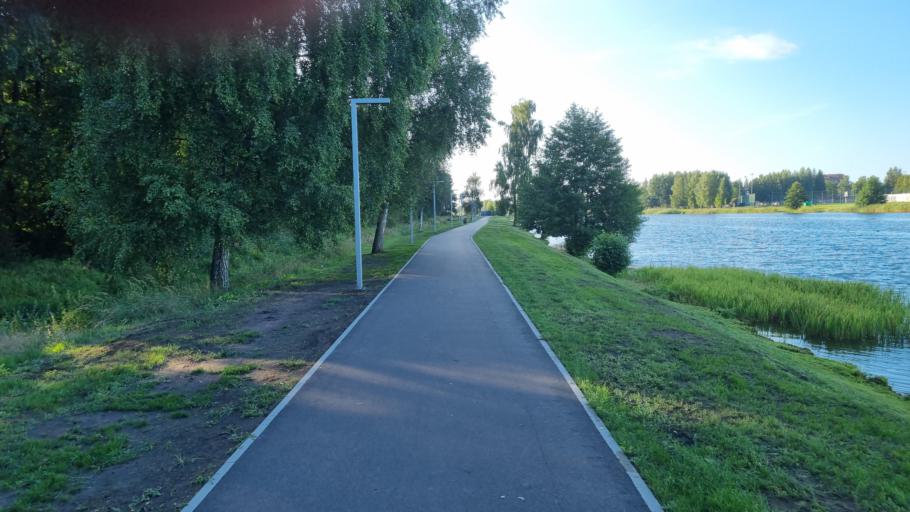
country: LV
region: Babite
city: Pinki
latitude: 56.9384
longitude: 23.9066
